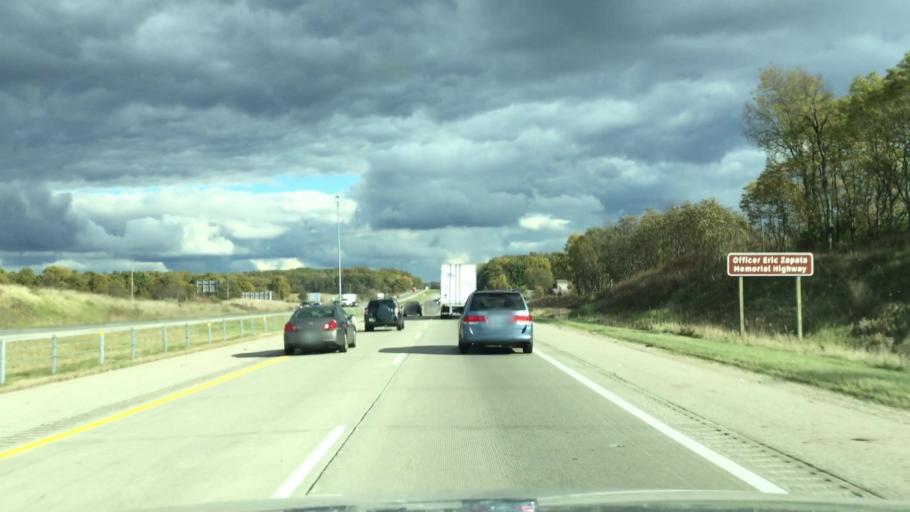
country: US
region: Michigan
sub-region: Van Buren County
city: Mattawan
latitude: 42.2230
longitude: -85.7625
